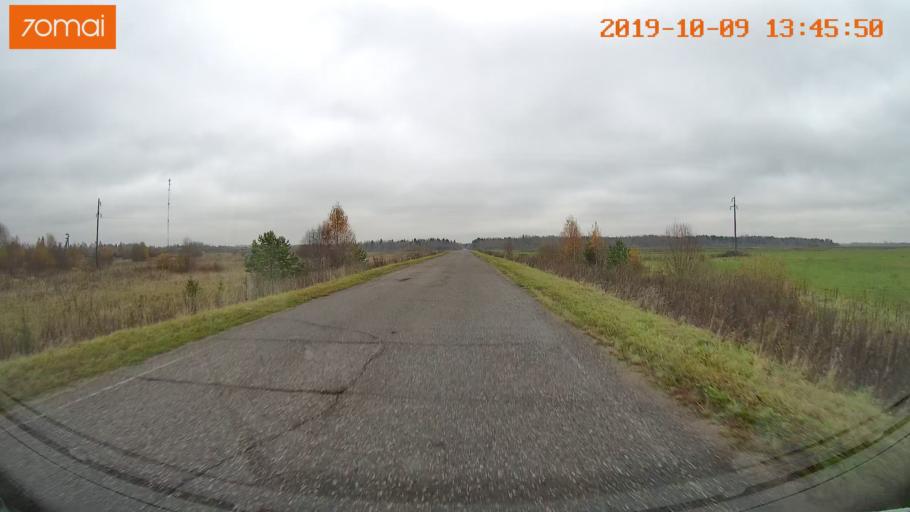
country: RU
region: Kostroma
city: Buy
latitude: 58.3780
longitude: 41.2132
